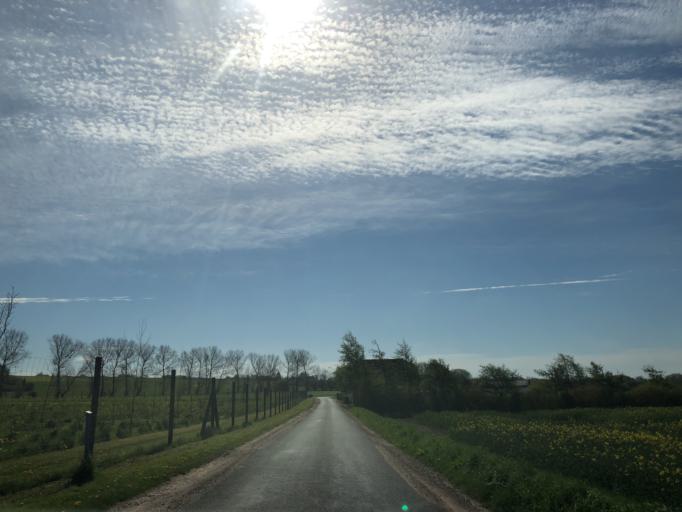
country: DK
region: Zealand
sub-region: Slagelse Kommune
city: Forlev
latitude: 55.3831
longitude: 11.2895
